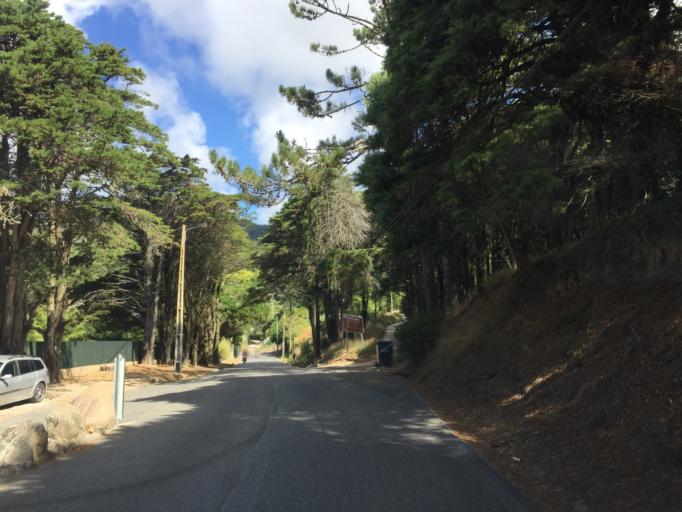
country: PT
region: Lisbon
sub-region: Sintra
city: Colares
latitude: 38.7578
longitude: -9.4448
